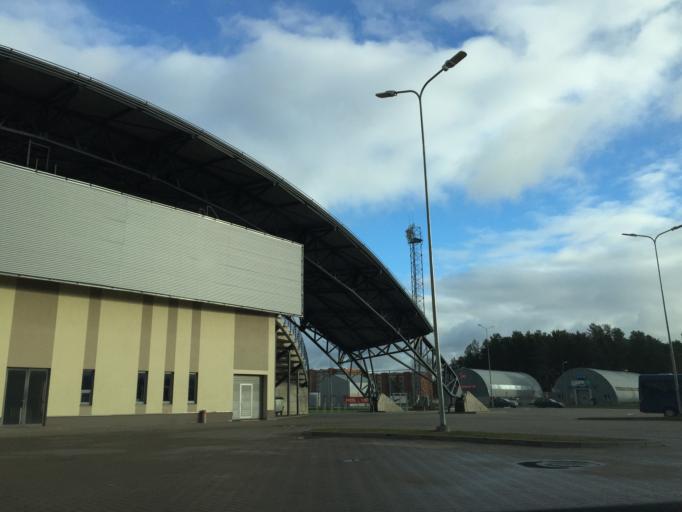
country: LV
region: Valmieras Rajons
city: Valmiera
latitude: 57.5285
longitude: 25.3891
